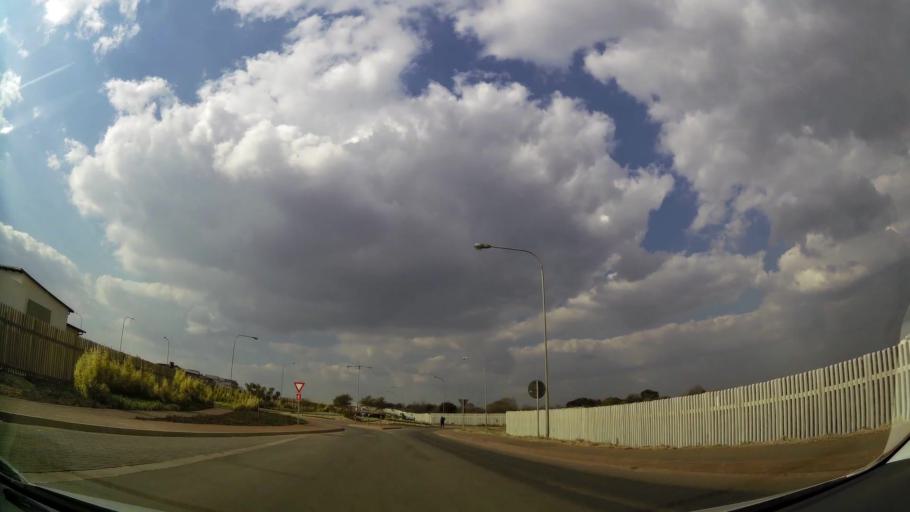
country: ZA
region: Gauteng
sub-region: Ekurhuleni Metropolitan Municipality
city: Tembisa
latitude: -25.9297
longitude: 28.2127
